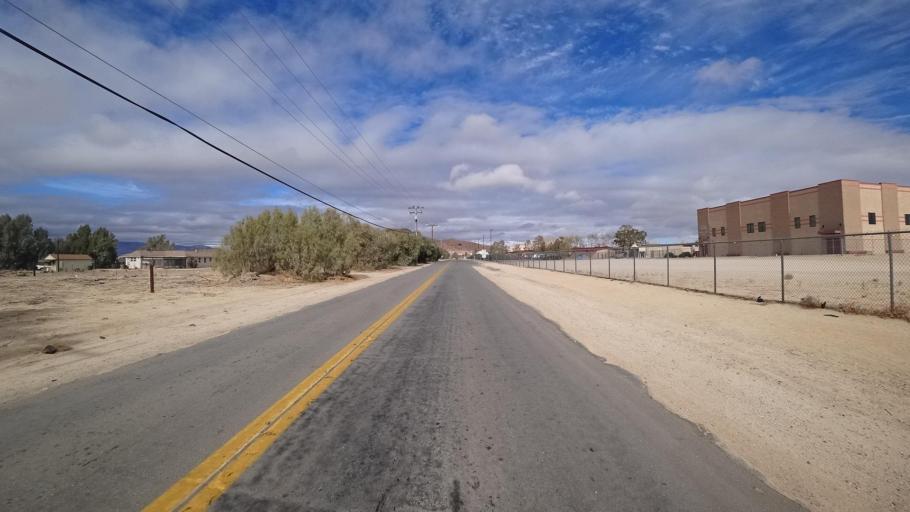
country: US
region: California
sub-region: Kern County
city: Rosamond
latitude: 34.8651
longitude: -118.2293
